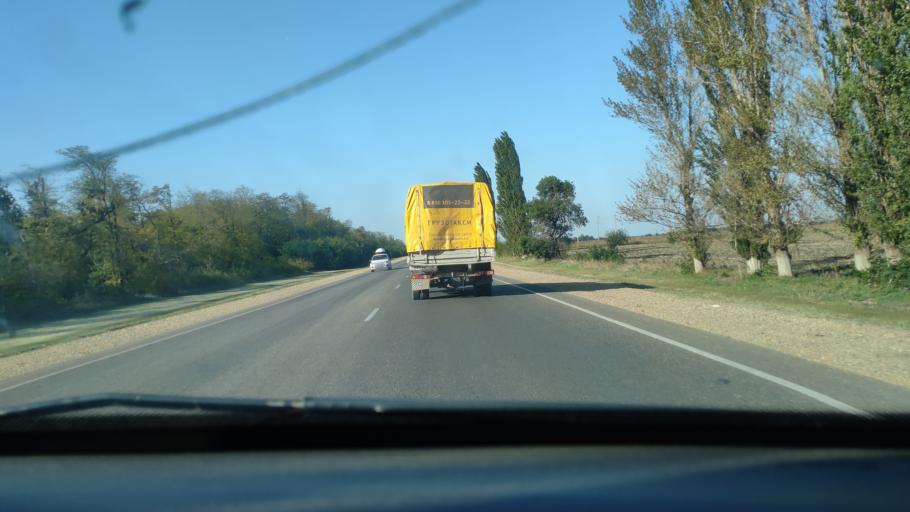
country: RU
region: Krasnodarskiy
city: Novotitarovskaya
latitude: 45.2666
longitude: 39.0022
